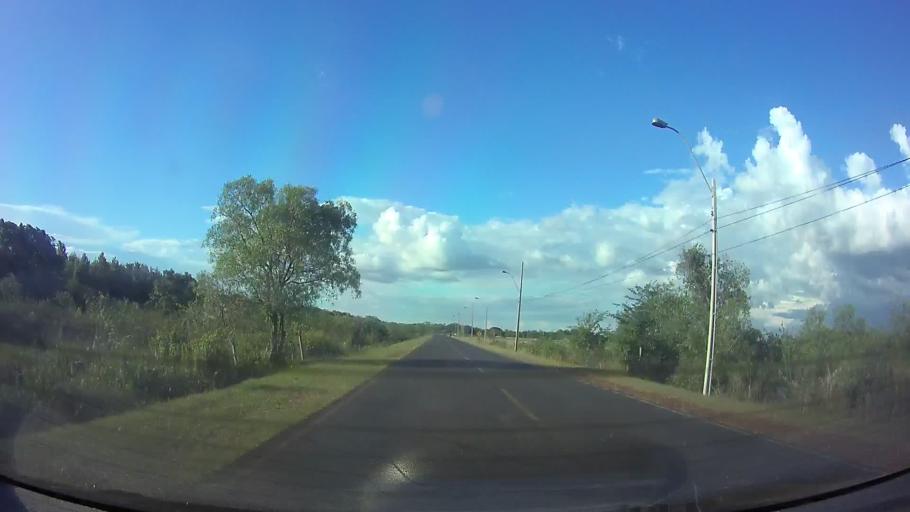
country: PY
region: Cordillera
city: Emboscada
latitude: -25.1481
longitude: -57.2605
